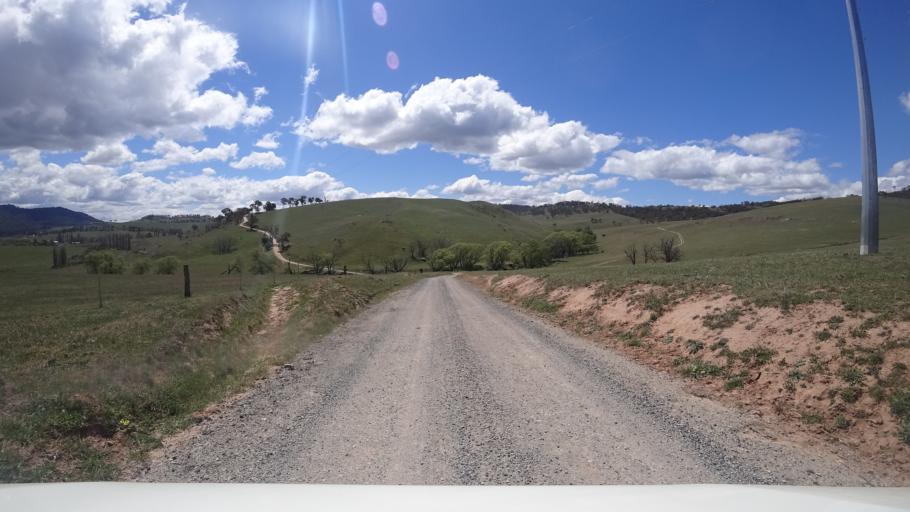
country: AU
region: New South Wales
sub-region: Oberon
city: Oberon
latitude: -33.5775
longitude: 149.9405
